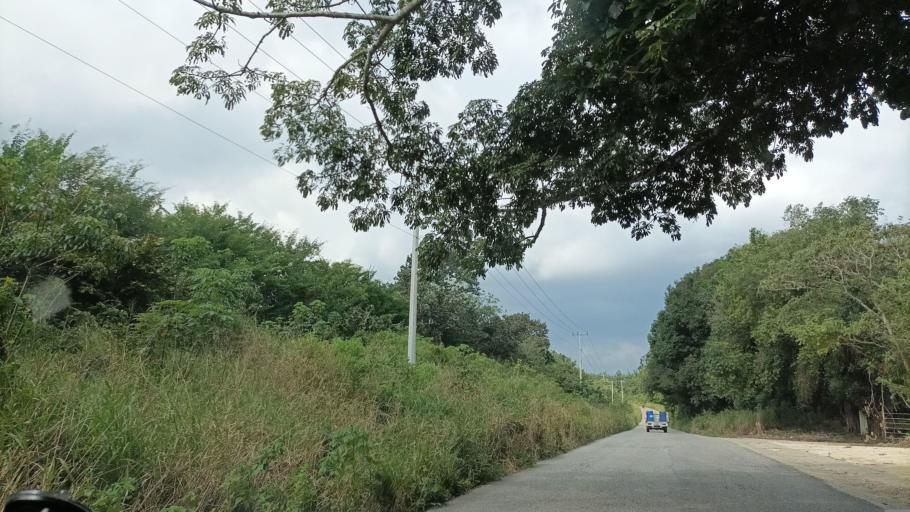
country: MX
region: Veracruz
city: Las Choapas
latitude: 17.8073
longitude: -94.1077
